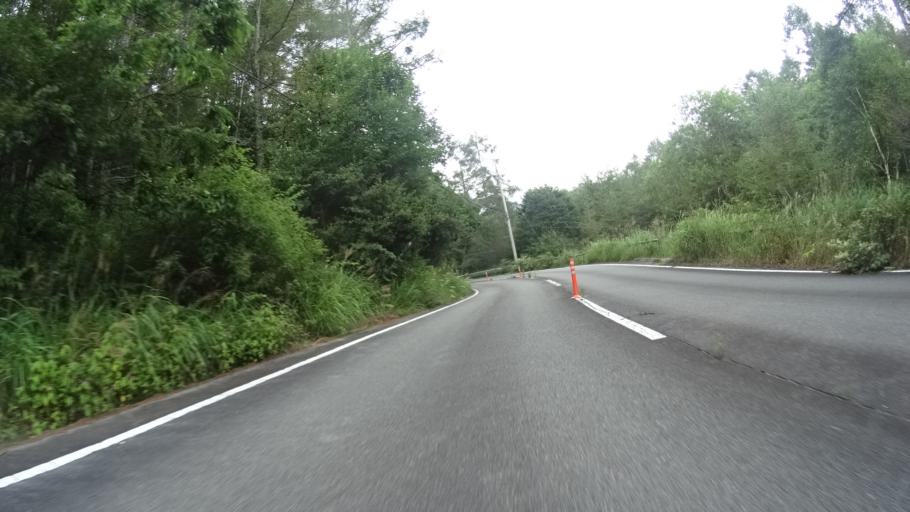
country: JP
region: Yamanashi
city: Enzan
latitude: 35.7974
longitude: 138.6492
